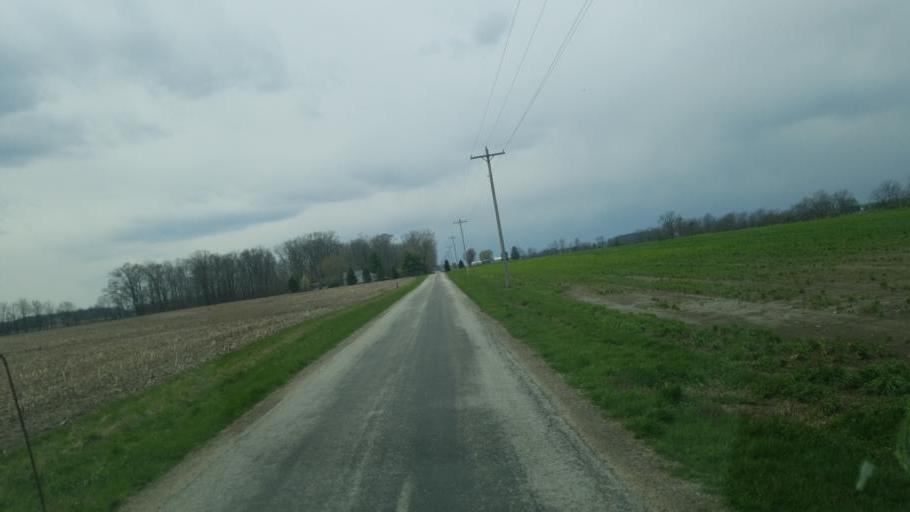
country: US
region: Ohio
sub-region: Marion County
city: Prospect
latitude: 40.3885
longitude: -83.2091
